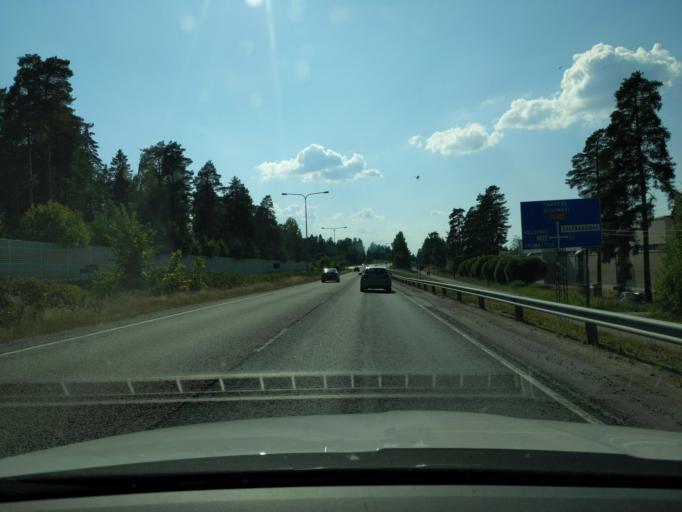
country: FI
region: Paijanne Tavastia
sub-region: Lahti
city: Hollola
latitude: 60.9874
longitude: 25.5429
